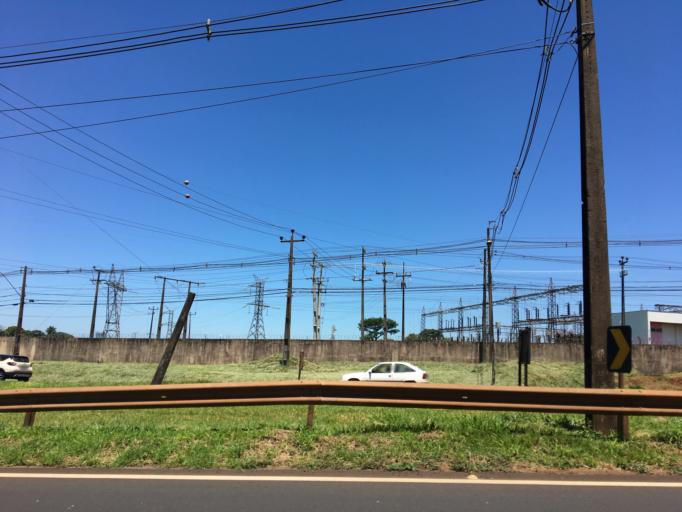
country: BR
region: Parana
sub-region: Maringa
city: Maringa
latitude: -23.4500
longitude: -51.9860
